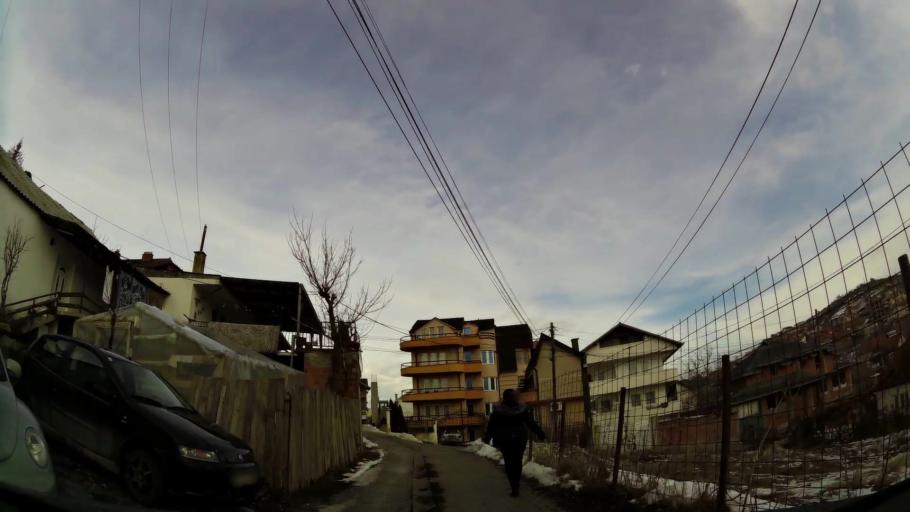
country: XK
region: Pristina
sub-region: Komuna e Prishtines
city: Pristina
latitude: 42.6717
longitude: 21.1844
